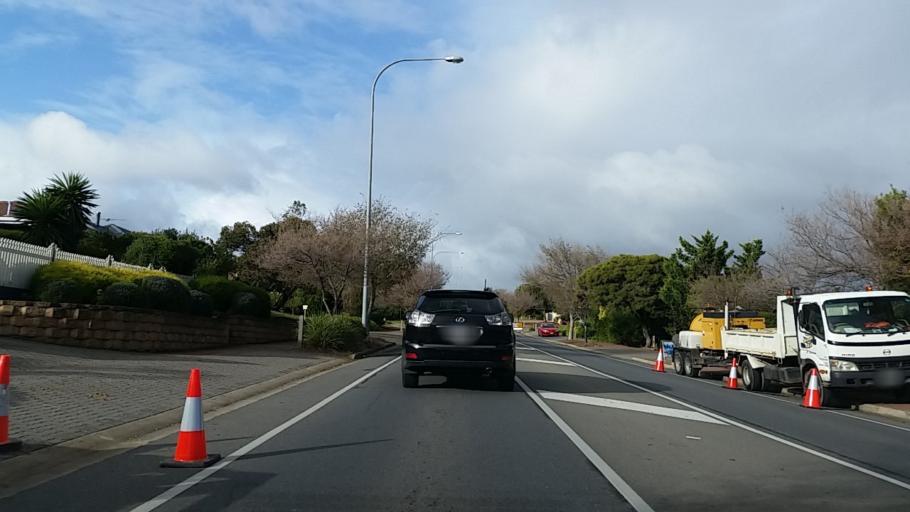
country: AU
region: South Australia
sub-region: Adelaide
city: Port Noarlunga
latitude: -35.1462
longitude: 138.4831
